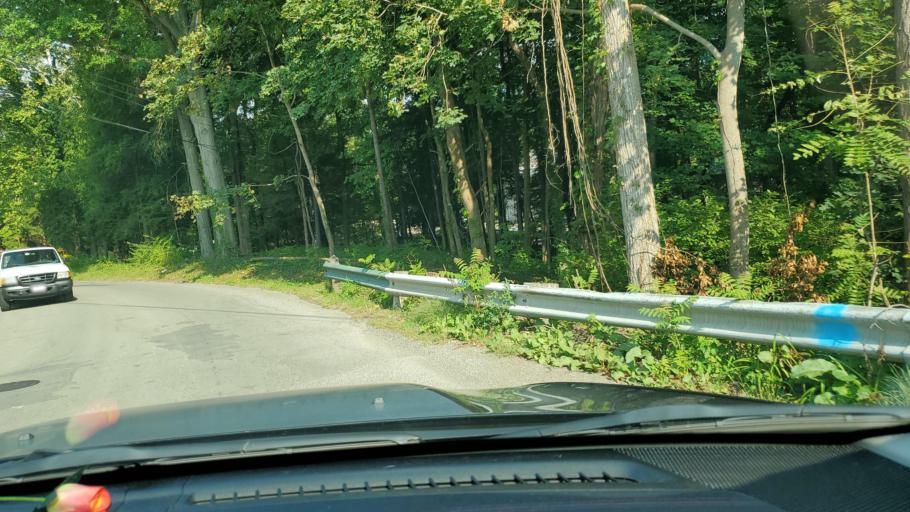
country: US
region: Ohio
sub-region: Mahoning County
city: Youngstown
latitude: 41.0848
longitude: -80.6779
